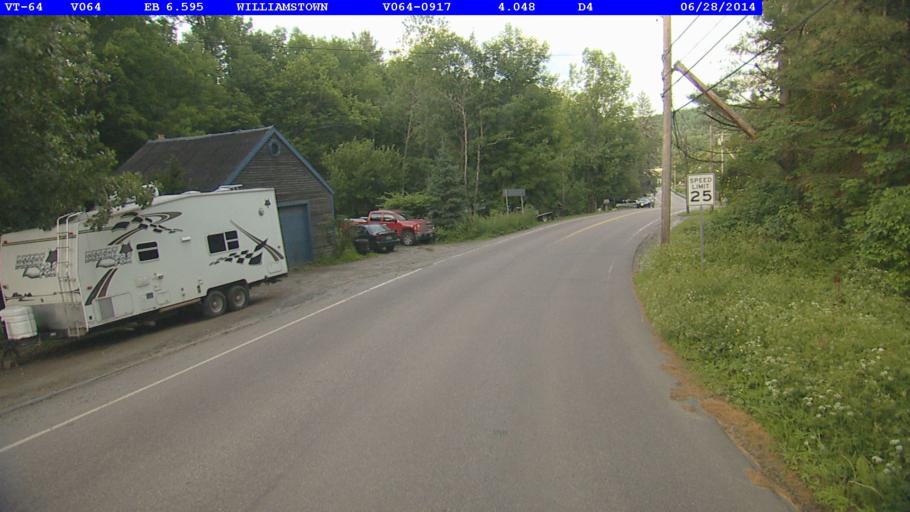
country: US
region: Vermont
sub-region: Orange County
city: Williamstown
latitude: 44.1221
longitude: -72.5447
